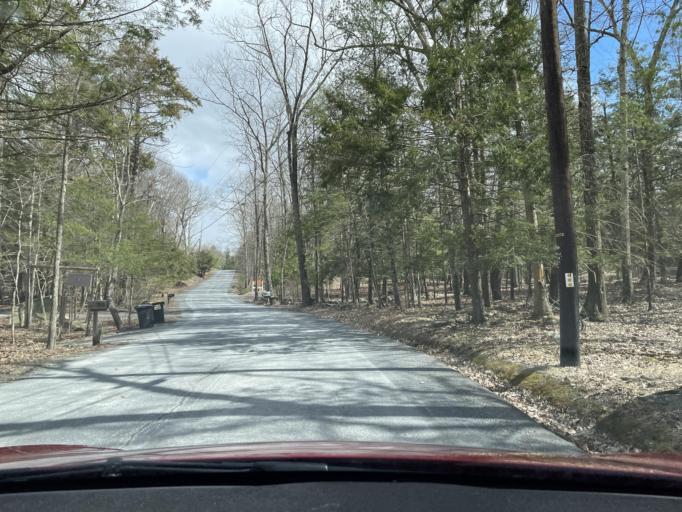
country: US
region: New York
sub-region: Ulster County
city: Zena
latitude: 42.0209
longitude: -74.0564
